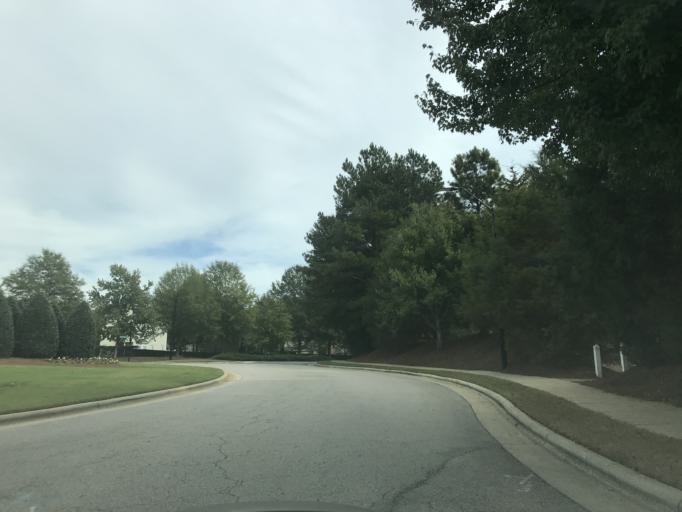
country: US
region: North Carolina
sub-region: Wake County
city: Wake Forest
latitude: 35.9638
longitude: -78.5505
